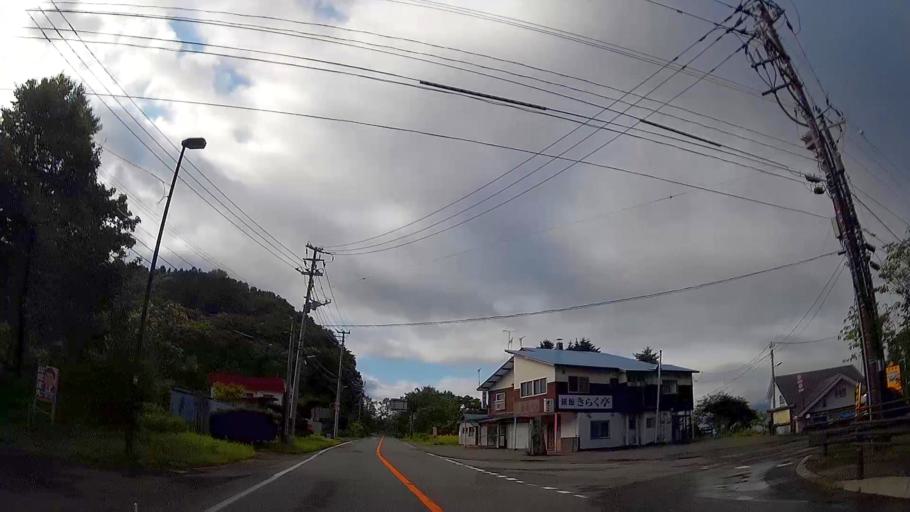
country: JP
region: Hokkaido
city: Date
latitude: 42.5624
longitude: 140.8849
